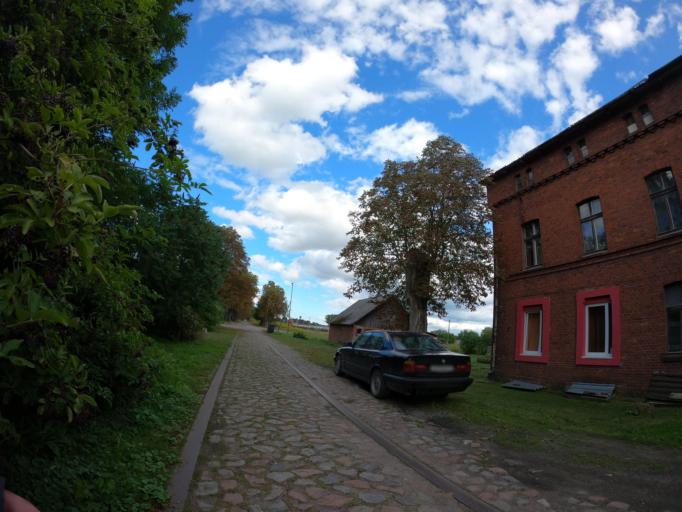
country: RU
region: Kaliningrad
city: Zheleznodorozhnyy
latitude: 54.3532
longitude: 21.3203
